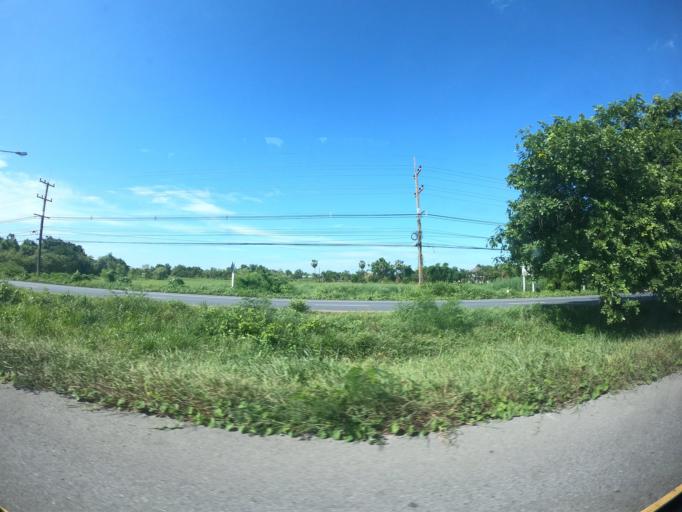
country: TH
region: Nakhon Nayok
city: Ban Na
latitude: 14.2426
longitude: 101.1160
